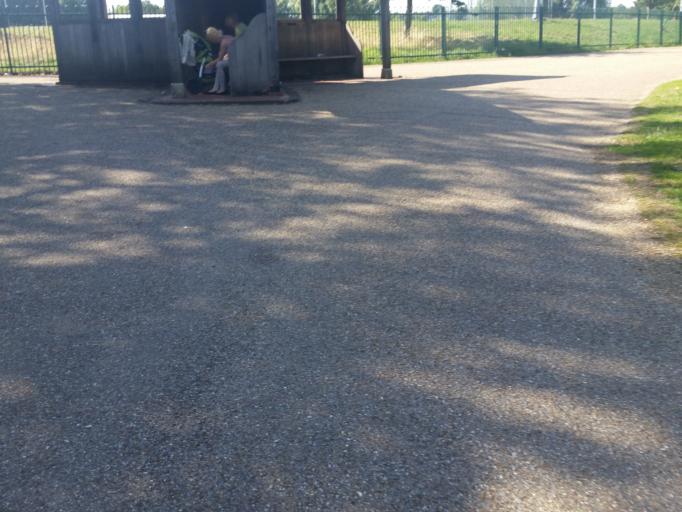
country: GB
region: England
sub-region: Greater London
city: Harringay
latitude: 51.5712
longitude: -0.0995
